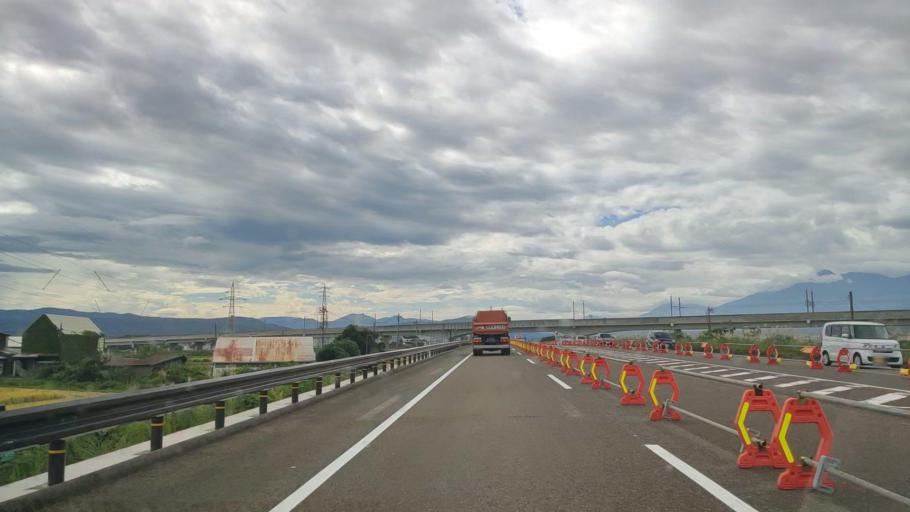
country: JP
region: Niigata
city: Arai
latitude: 37.0707
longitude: 138.2643
